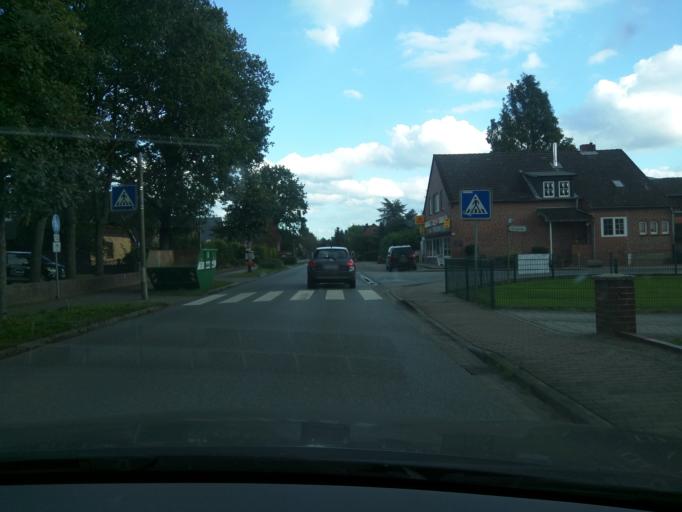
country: DE
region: Lower Saxony
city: Marschacht
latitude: 53.4162
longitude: 10.3715
